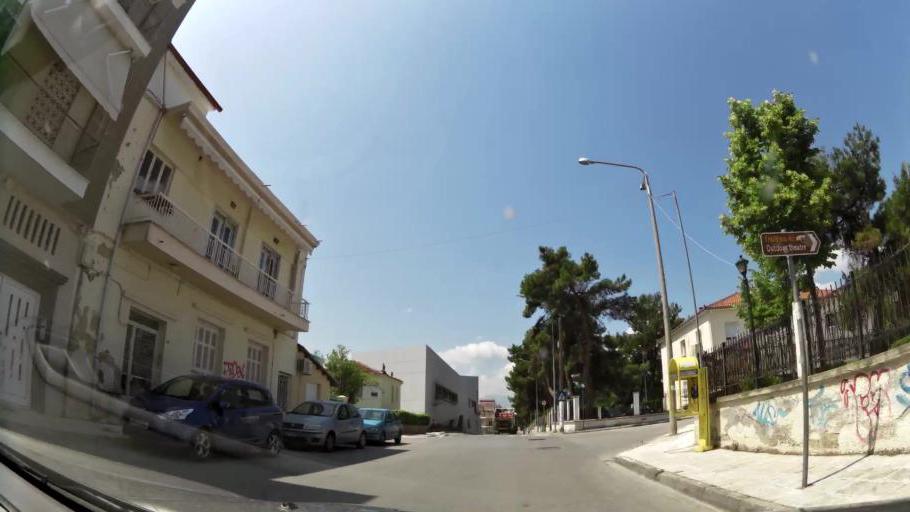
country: GR
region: West Macedonia
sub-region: Nomos Kozanis
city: Kozani
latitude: 40.2969
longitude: 21.7840
